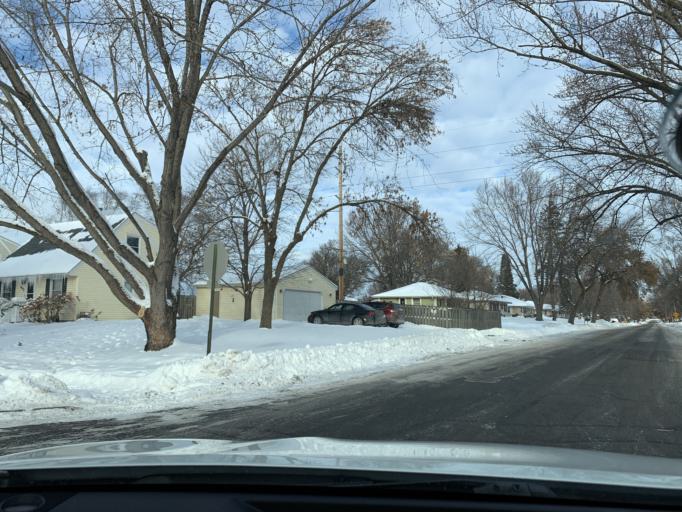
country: US
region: Minnesota
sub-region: Anoka County
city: Blaine
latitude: 45.1679
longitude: -93.2817
